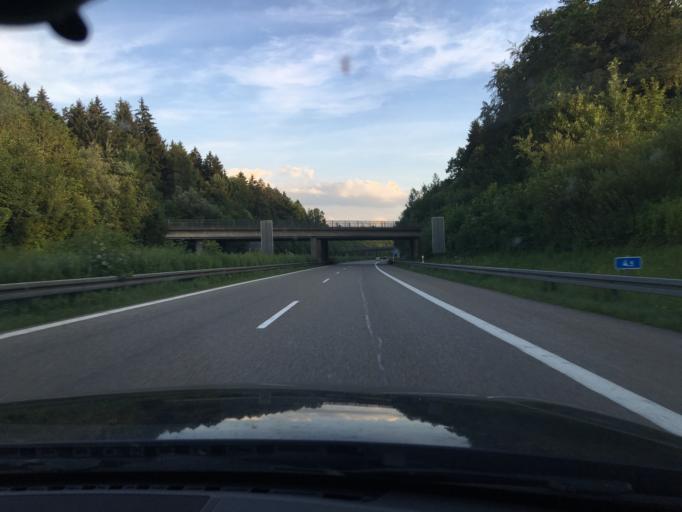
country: DE
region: Bavaria
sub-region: Swabia
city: Weissensberg
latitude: 47.5873
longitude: 9.7361
